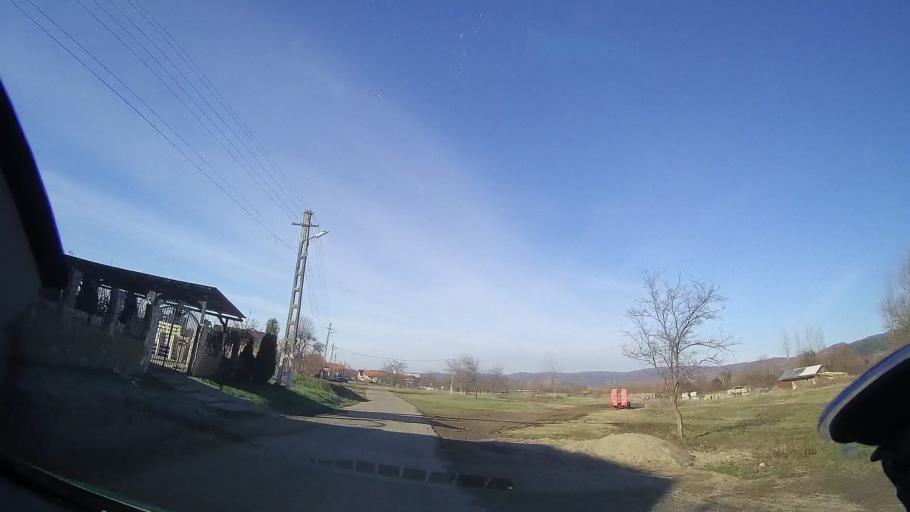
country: RO
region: Bihor
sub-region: Comuna Auseu
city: Auseu
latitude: 47.0232
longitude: 22.4930
